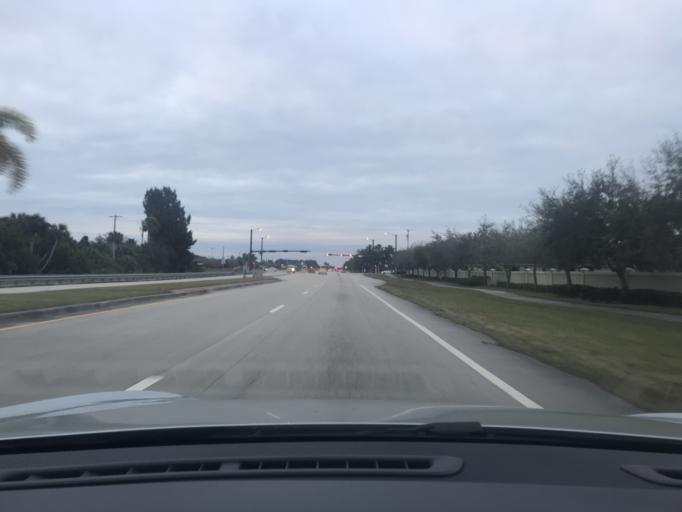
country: US
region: Florida
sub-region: Indian River County
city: West Vero Corridor
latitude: 27.6479
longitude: -80.4633
